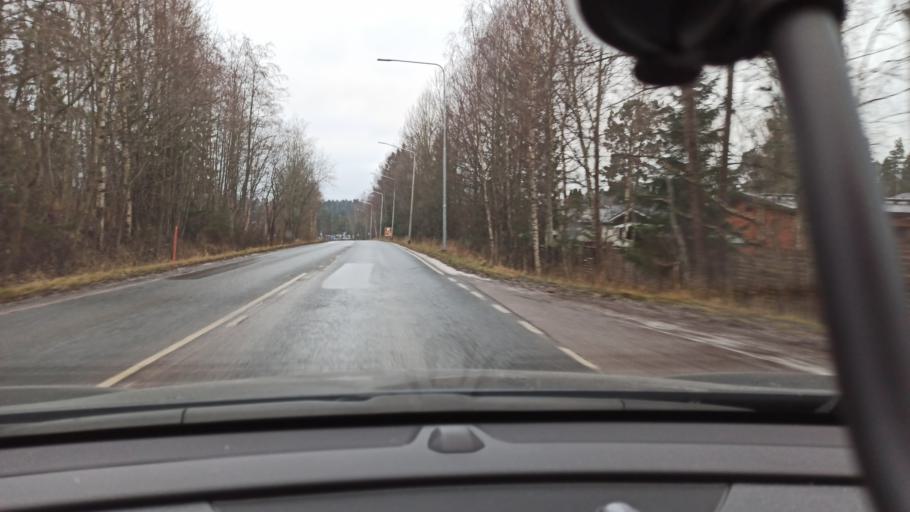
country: FI
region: Uusimaa
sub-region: Helsinki
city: Kirkkonummi
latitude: 60.1369
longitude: 24.4463
